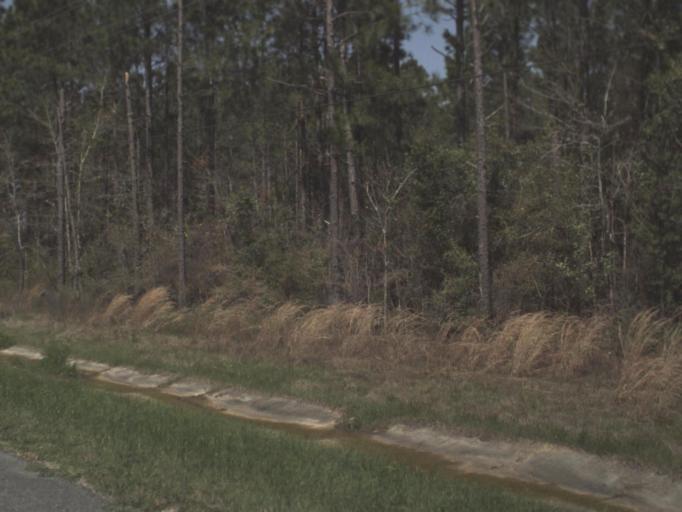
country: US
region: Alabama
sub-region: Geneva County
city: Geneva
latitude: 30.9542
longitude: -85.8855
